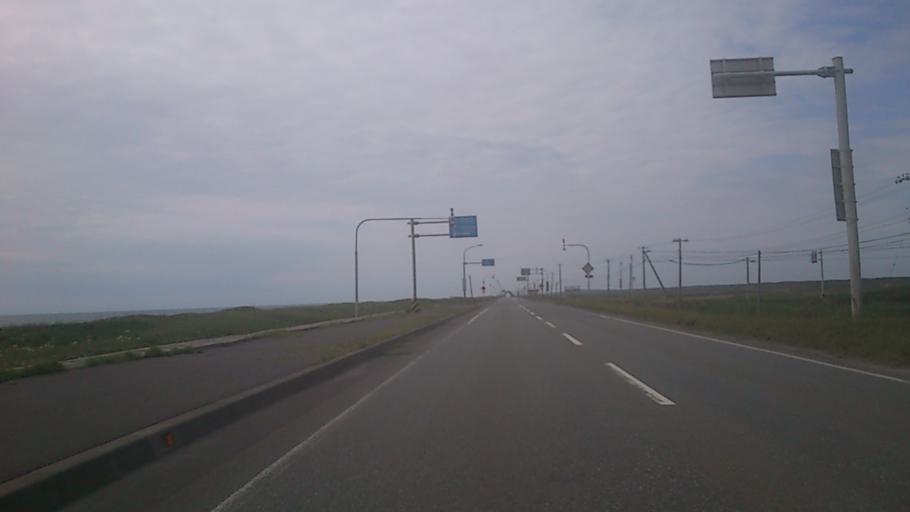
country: JP
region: Hokkaido
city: Makubetsu
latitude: 44.9927
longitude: 141.6867
